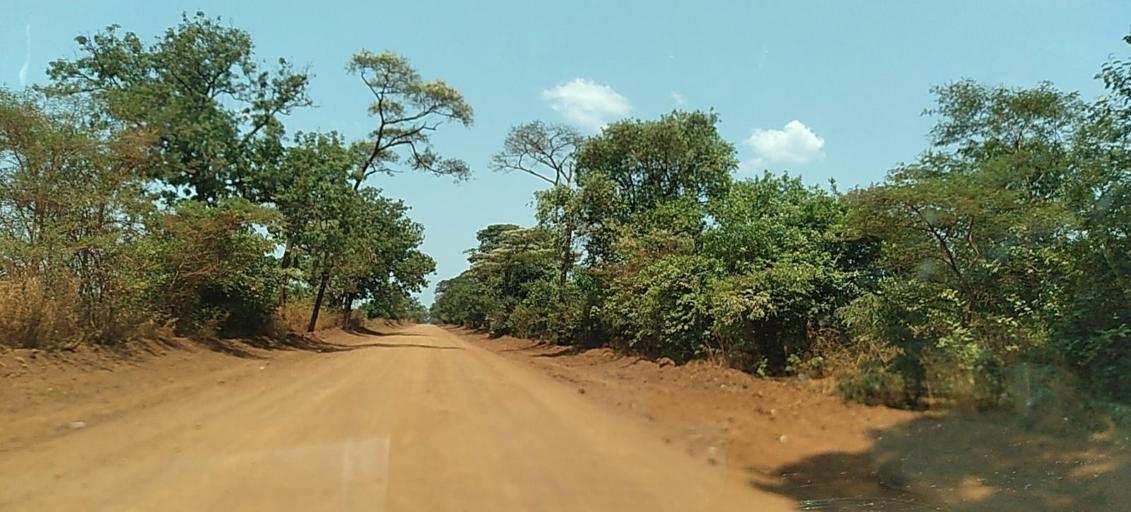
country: ZM
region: Copperbelt
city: Mpongwe
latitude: -13.5148
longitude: 28.0189
